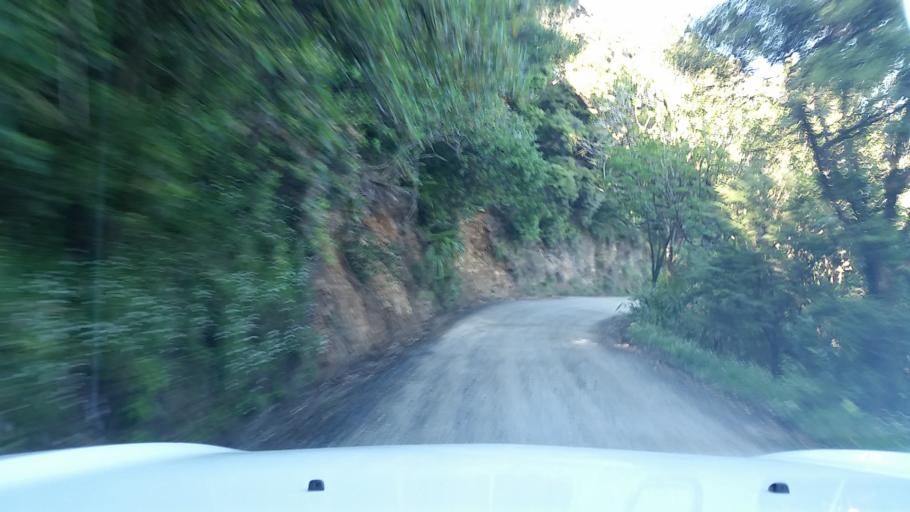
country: NZ
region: Auckland
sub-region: Auckland
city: Titirangi
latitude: -37.0284
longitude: 174.5270
